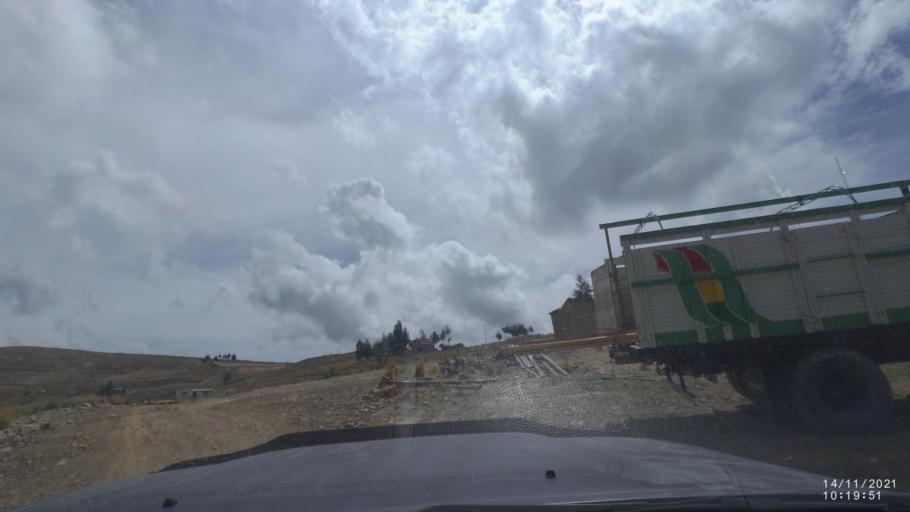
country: BO
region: Cochabamba
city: Cochabamba
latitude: -17.3343
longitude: -66.0823
